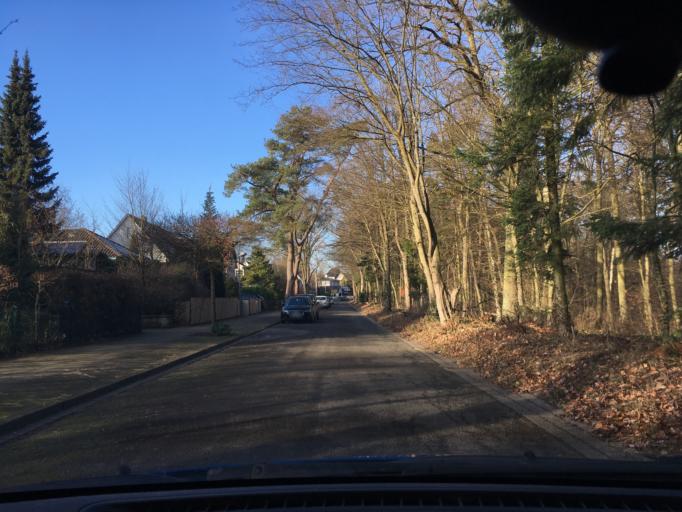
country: DE
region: Lower Saxony
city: Lueneburg
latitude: 53.2228
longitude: 10.4111
